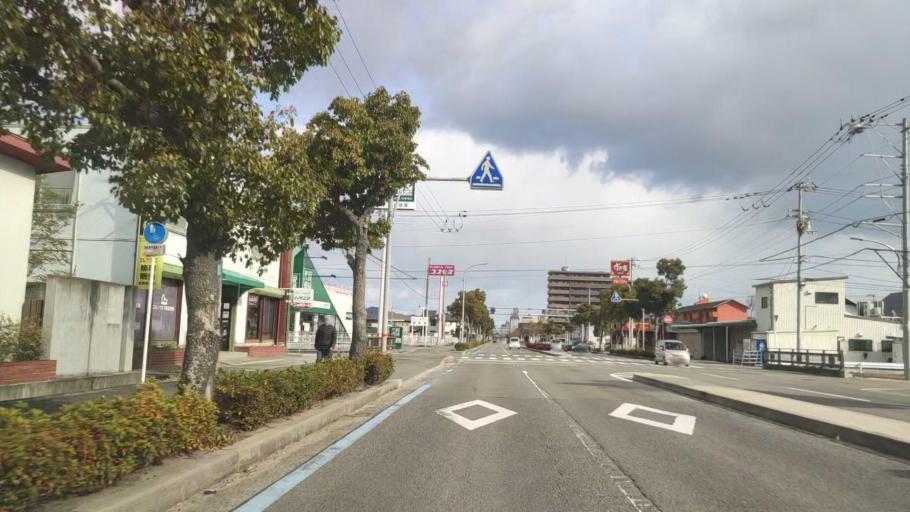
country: JP
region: Ehime
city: Hojo
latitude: 34.0595
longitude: 132.9828
